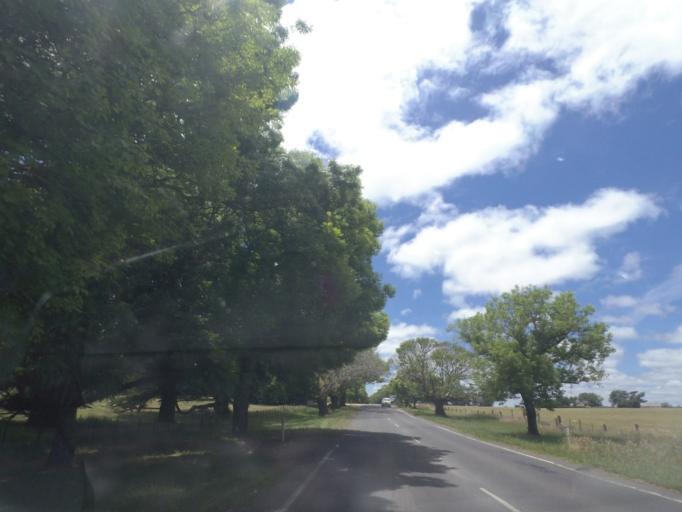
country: AU
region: Victoria
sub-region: Mount Alexander
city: Castlemaine
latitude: -37.3385
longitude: 144.1597
